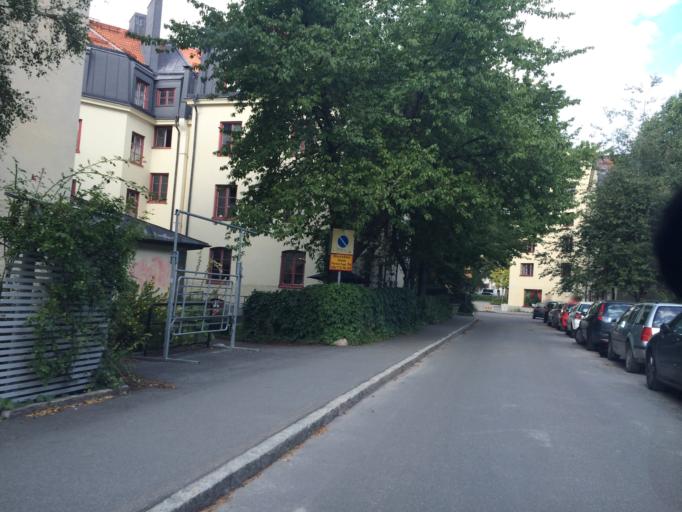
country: SE
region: Stockholm
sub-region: Stockholms Kommun
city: Arsta
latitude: 59.3050
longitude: 18.0021
